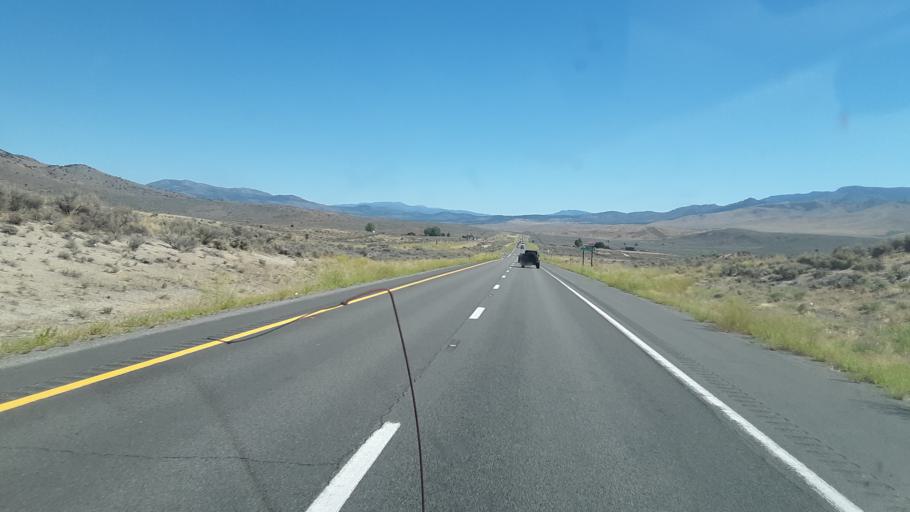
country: US
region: Nevada
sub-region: Washoe County
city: Cold Springs
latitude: 39.7414
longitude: -120.0398
